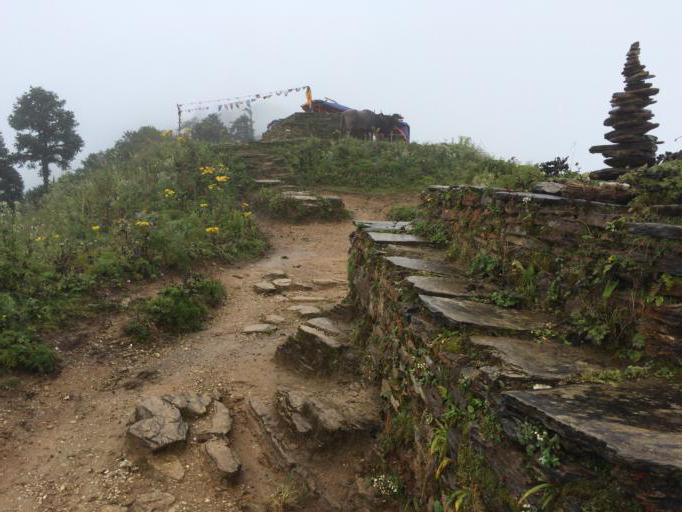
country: NP
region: Western Region
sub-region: Dhawalagiri Zone
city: Chitre
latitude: 28.3956
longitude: 83.7125
